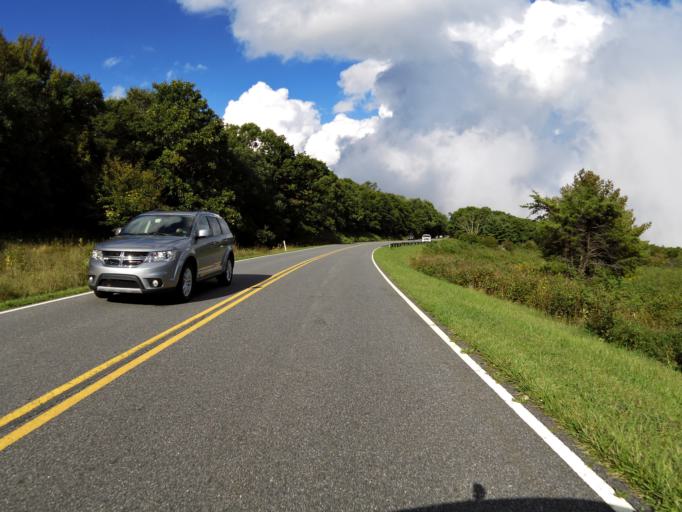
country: US
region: Virginia
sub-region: Page County
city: Stanley
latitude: 38.5447
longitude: -78.3916
